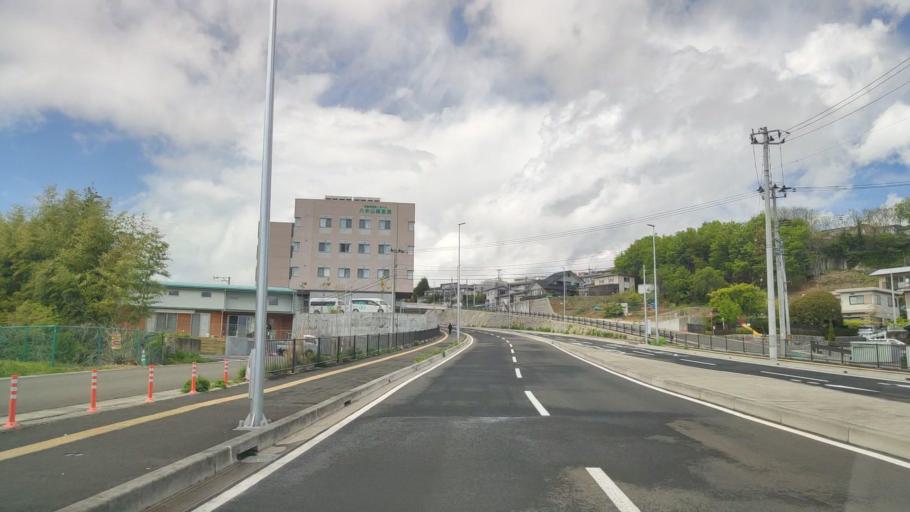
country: JP
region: Miyagi
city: Sendai
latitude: 38.2340
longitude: 140.8527
